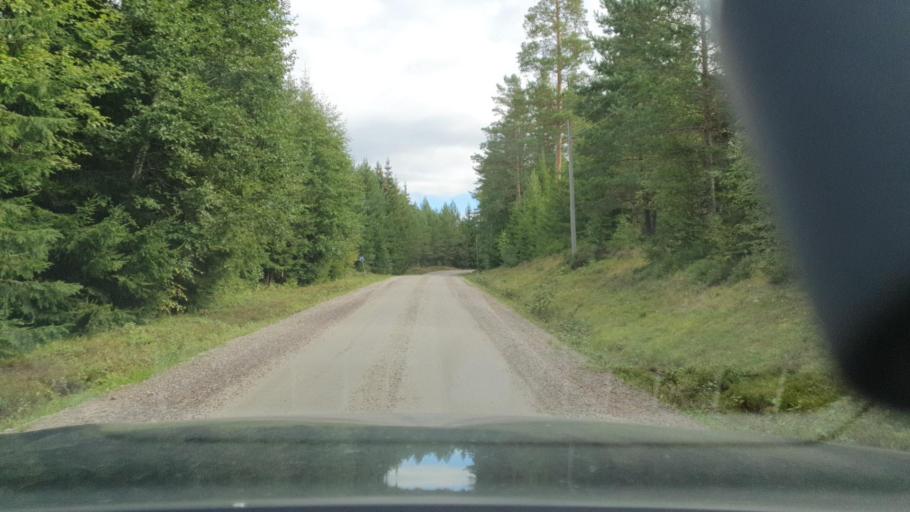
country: SE
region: Vaermland
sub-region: Hagfors Kommun
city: Ekshaerad
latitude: 60.2008
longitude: 13.5414
